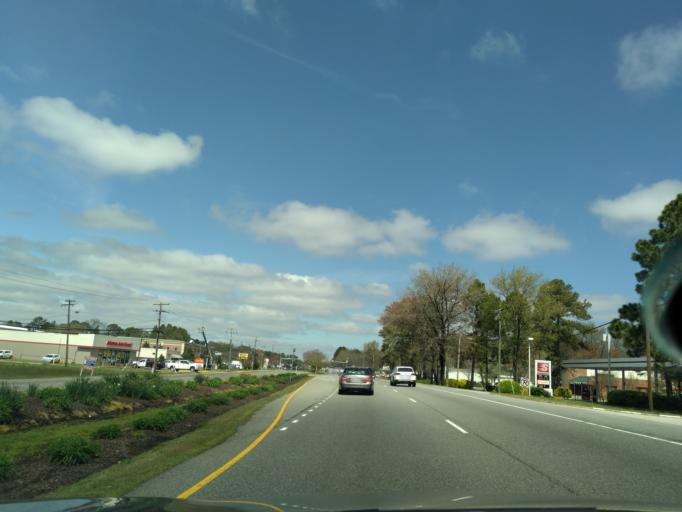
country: US
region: Virginia
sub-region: City of Poquoson
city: Poquoson
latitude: 37.1080
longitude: -76.4559
